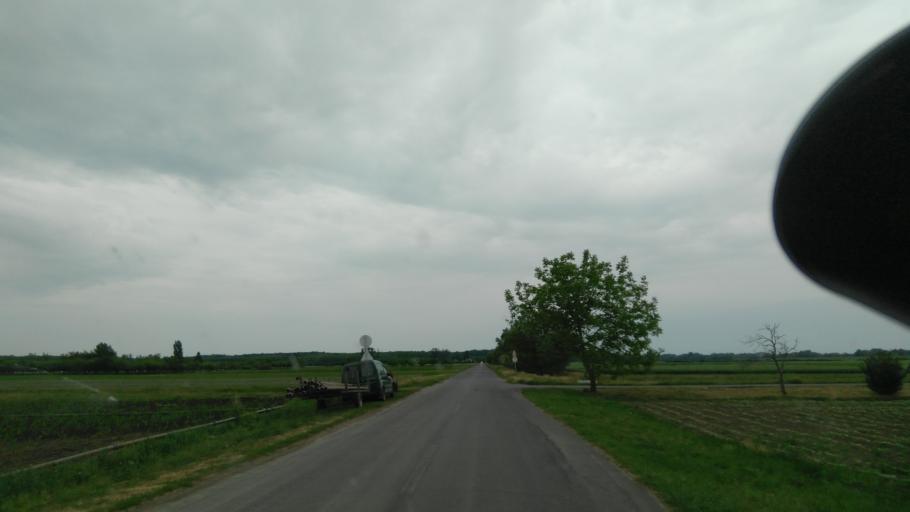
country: HU
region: Bekes
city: Doboz
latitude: 46.7226
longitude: 21.2444
